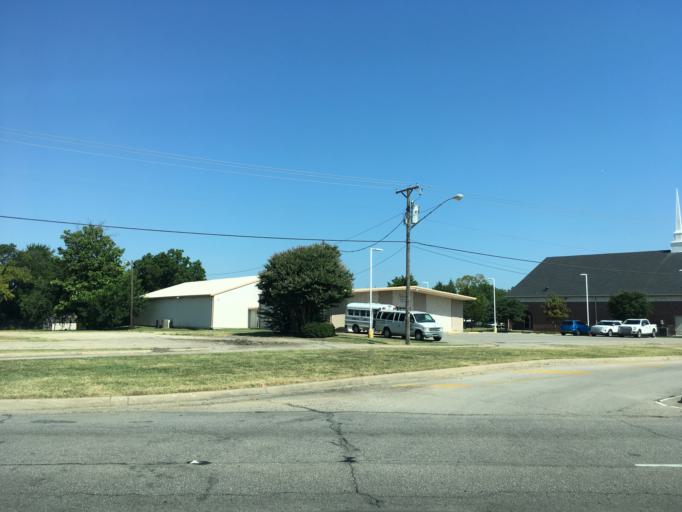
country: US
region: Texas
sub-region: Collin County
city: McKinney
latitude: 33.1813
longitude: -96.6179
